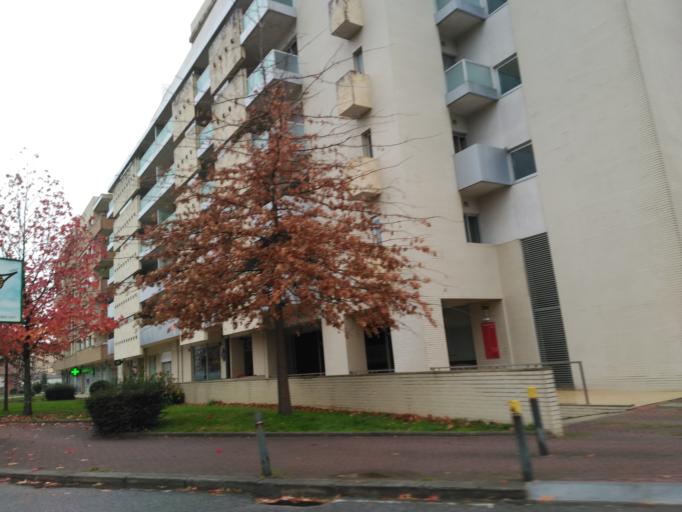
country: PT
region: Braga
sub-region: Braga
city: Braga
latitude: 41.5531
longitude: -8.4000
